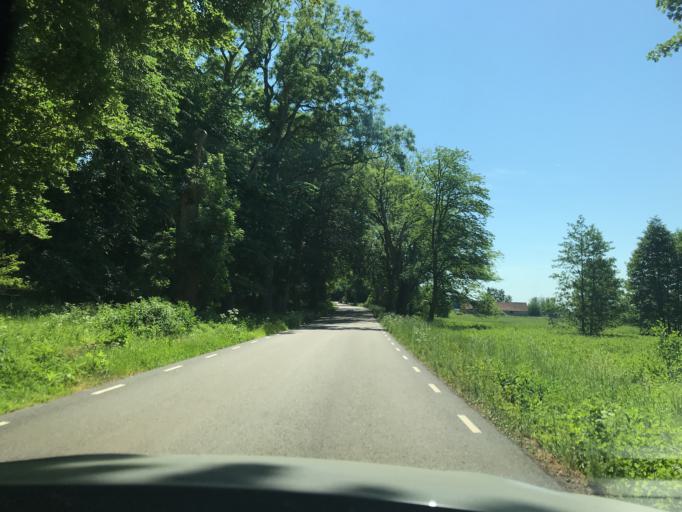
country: SE
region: Vaestra Goetaland
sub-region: Gotene Kommun
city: Kallby
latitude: 58.5817
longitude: 13.3731
